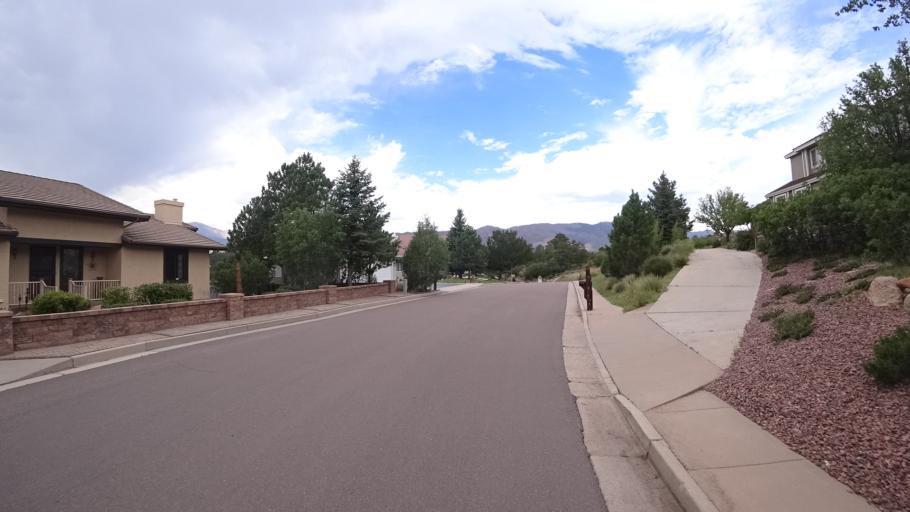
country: US
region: Colorado
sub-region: El Paso County
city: Colorado Springs
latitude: 38.9107
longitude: -104.8413
